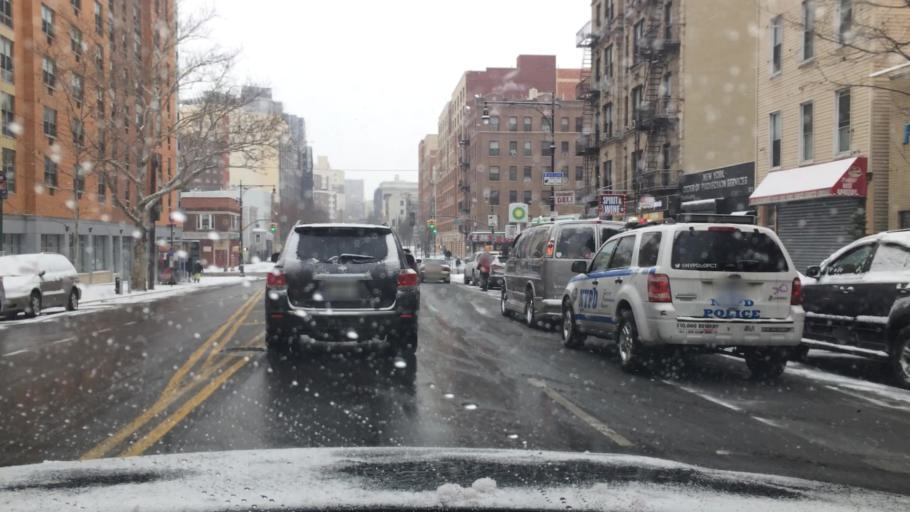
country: US
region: New York
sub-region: New York County
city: Inwood
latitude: 40.8246
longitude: -73.9148
